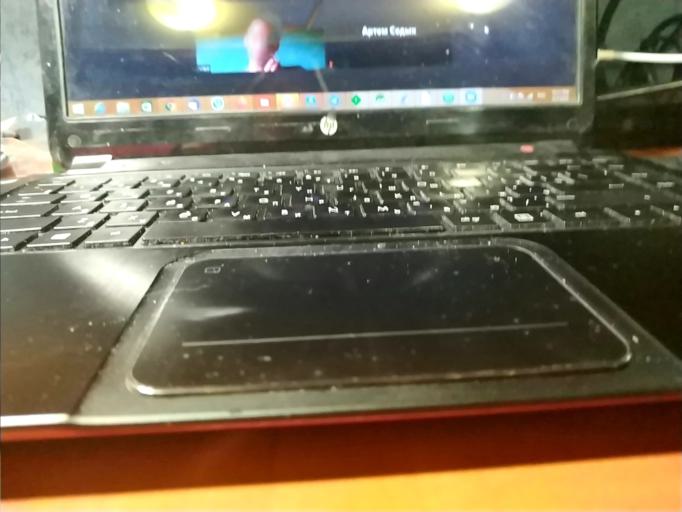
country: RU
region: Tverskaya
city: Ves'yegonsk
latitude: 58.6974
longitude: 37.5440
